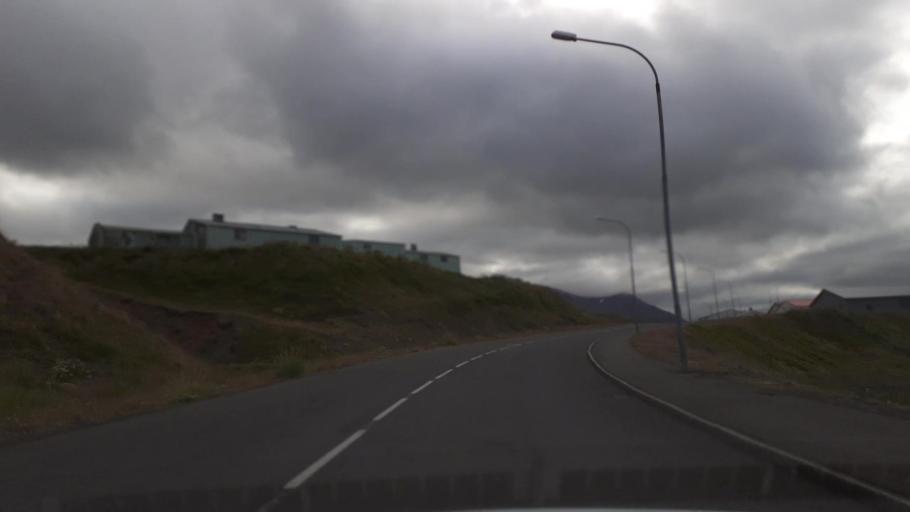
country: IS
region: Northeast
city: Akureyri
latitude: 65.9539
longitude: -18.1825
